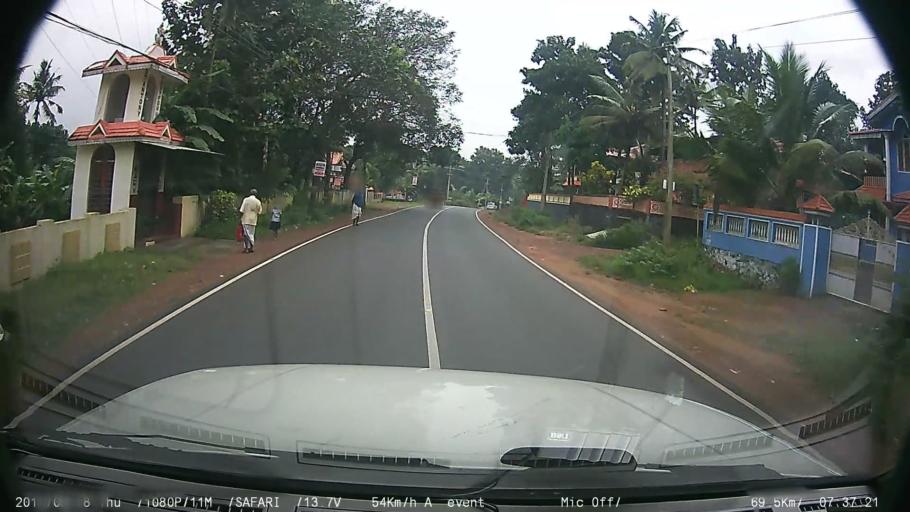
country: IN
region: Kerala
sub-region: Kottayam
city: Changanacheri
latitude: 9.4338
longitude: 76.5665
